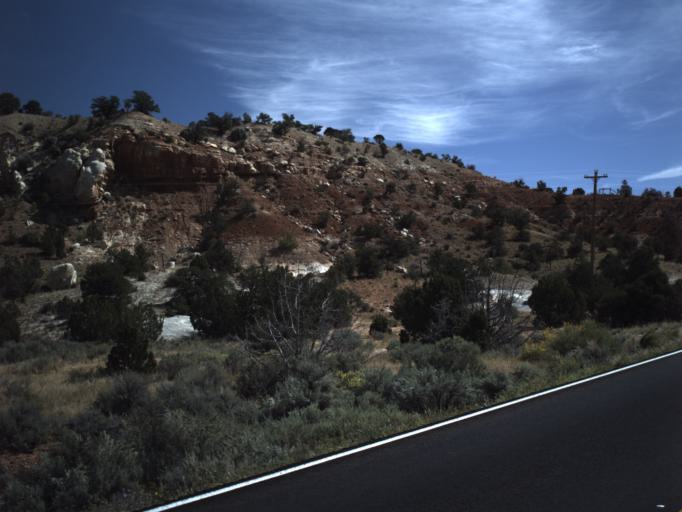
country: US
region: Utah
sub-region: Wayne County
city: Loa
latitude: 37.7758
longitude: -111.6187
